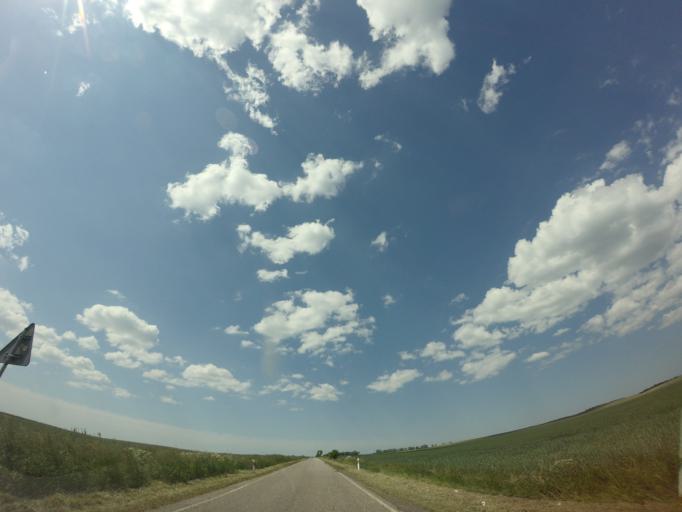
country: PL
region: West Pomeranian Voivodeship
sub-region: Powiat stargardzki
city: Dolice
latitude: 53.1650
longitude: 15.2280
